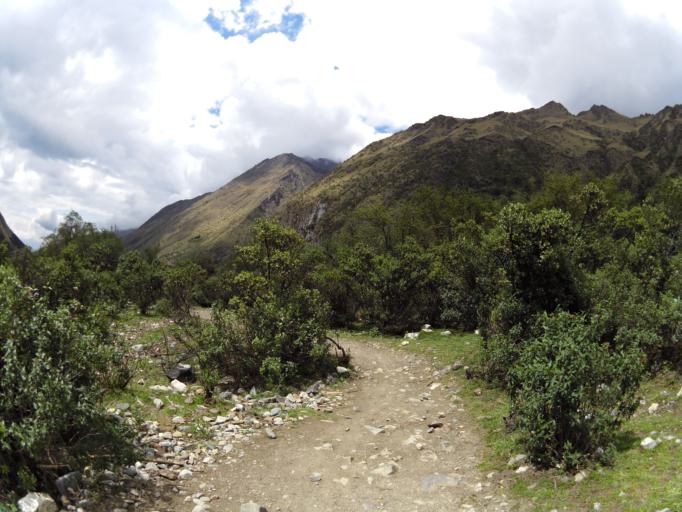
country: PE
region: Cusco
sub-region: Provincia de Anta
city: Limatambo
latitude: -13.3897
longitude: -72.5739
